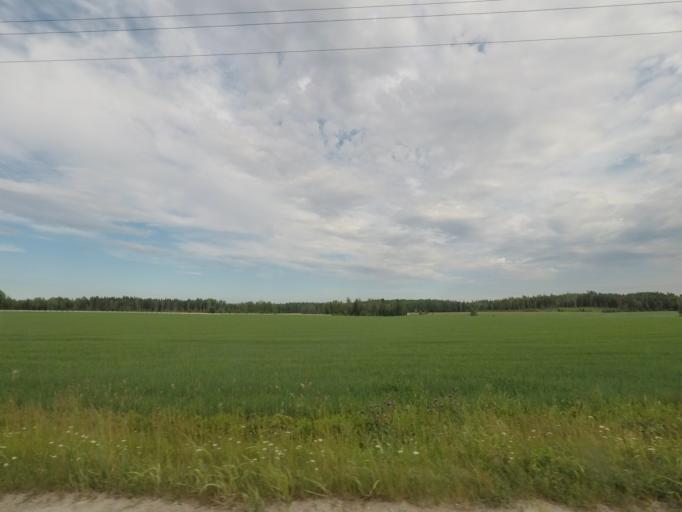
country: FI
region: Paijanne Tavastia
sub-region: Lahti
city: Lahti
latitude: 60.9264
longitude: 25.5799
